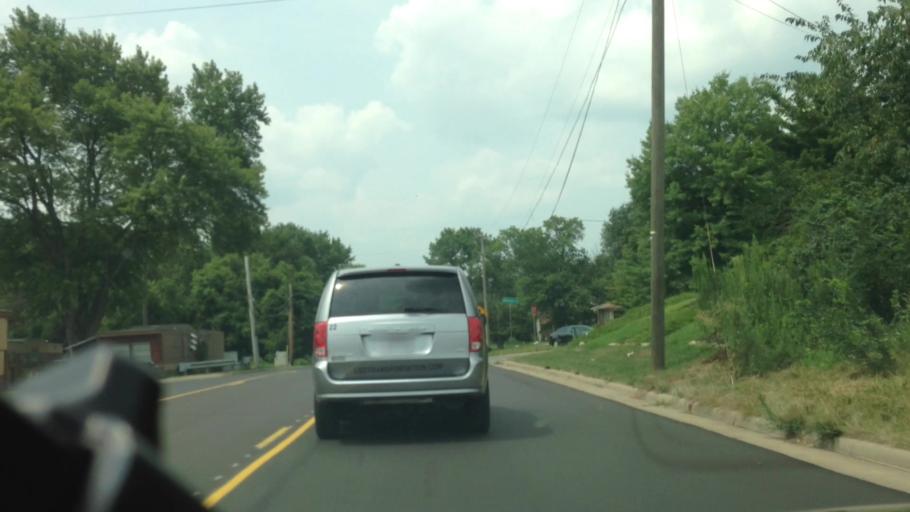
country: US
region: Ohio
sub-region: Stark County
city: Genoa
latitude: 40.8109
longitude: -81.4273
